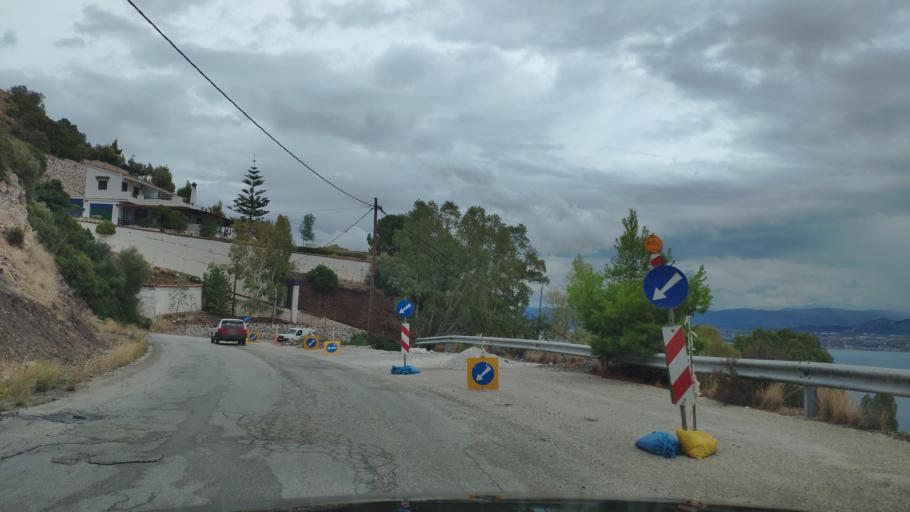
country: GR
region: Peloponnese
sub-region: Nomos Korinthias
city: Perachora
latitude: 38.0029
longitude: 22.9401
